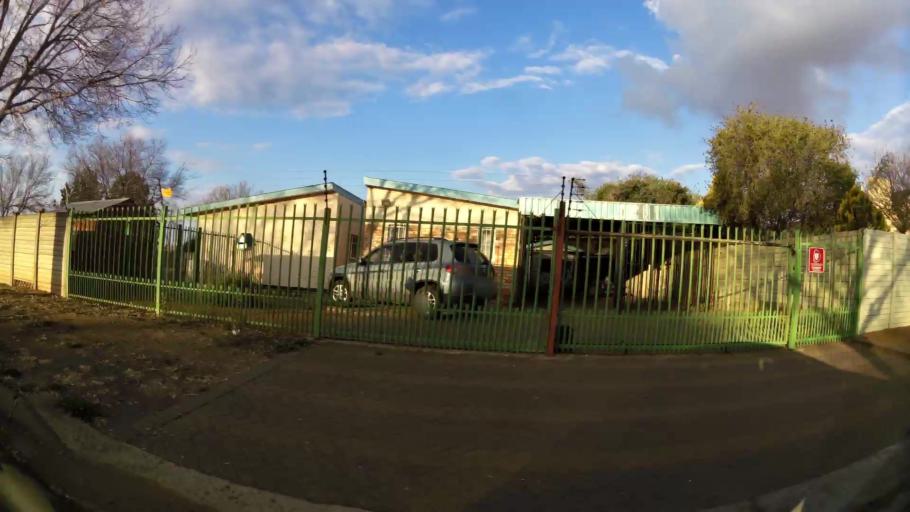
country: ZA
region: Orange Free State
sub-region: Mangaung Metropolitan Municipality
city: Bloemfontein
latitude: -29.1347
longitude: 26.1850
